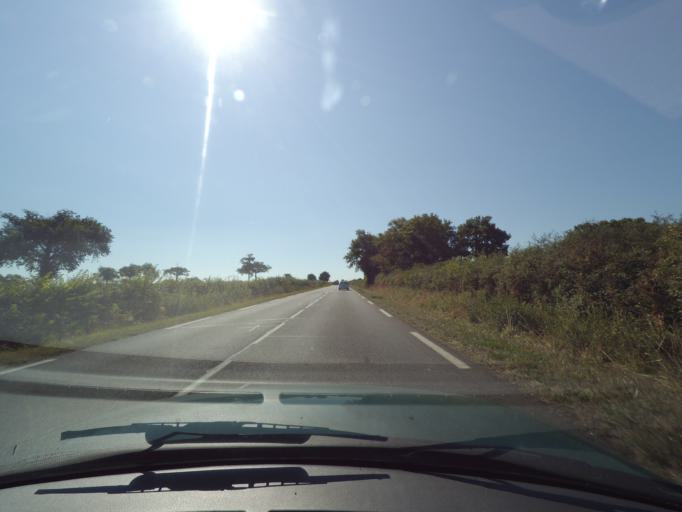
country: FR
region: Limousin
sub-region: Departement de la Haute-Vienne
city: Peyrat-de-Bellac
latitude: 46.1417
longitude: 0.9766
